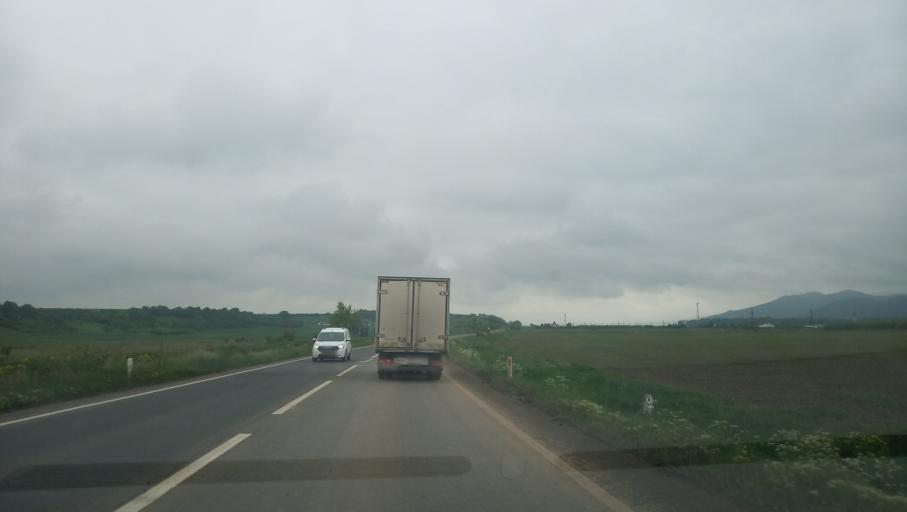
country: RO
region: Alba
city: Vurpar
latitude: 45.9725
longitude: 23.4600
